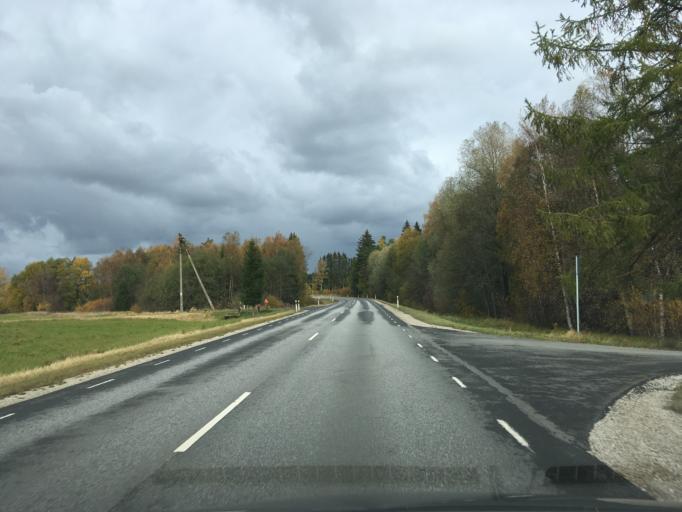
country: EE
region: Harju
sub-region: Anija vald
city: Kehra
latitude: 59.2898
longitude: 25.3755
